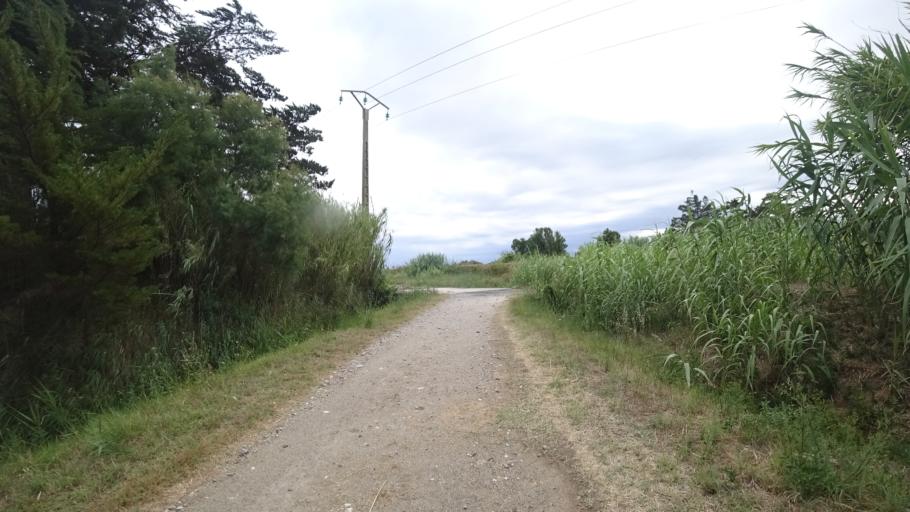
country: FR
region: Languedoc-Roussillon
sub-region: Departement des Pyrenees-Orientales
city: Le Barcares
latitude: 42.7779
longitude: 3.0163
